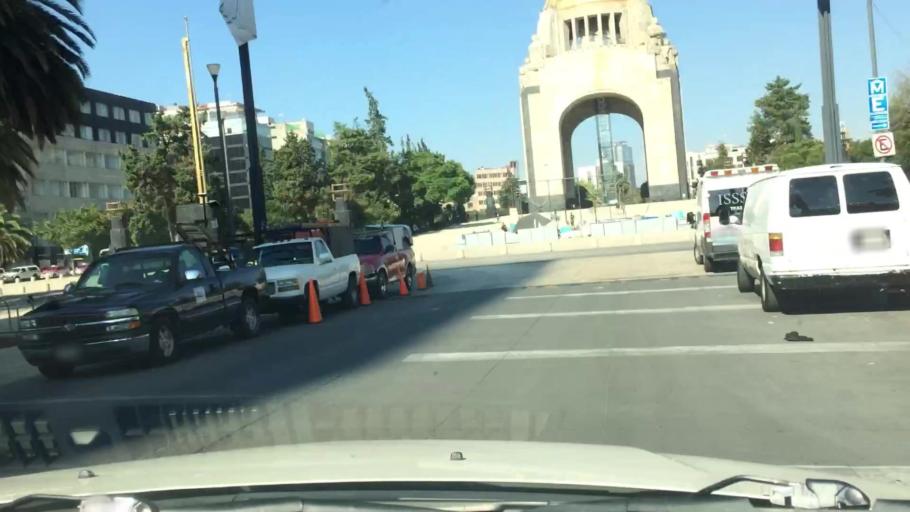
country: MX
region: Mexico City
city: Cuauhtemoc
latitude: 19.4360
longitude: -99.1527
